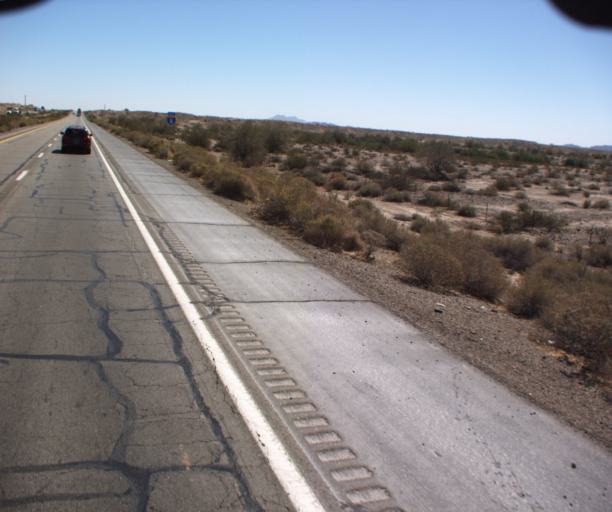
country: US
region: Arizona
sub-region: Yuma County
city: Wellton
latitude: 32.6637
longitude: -114.2706
